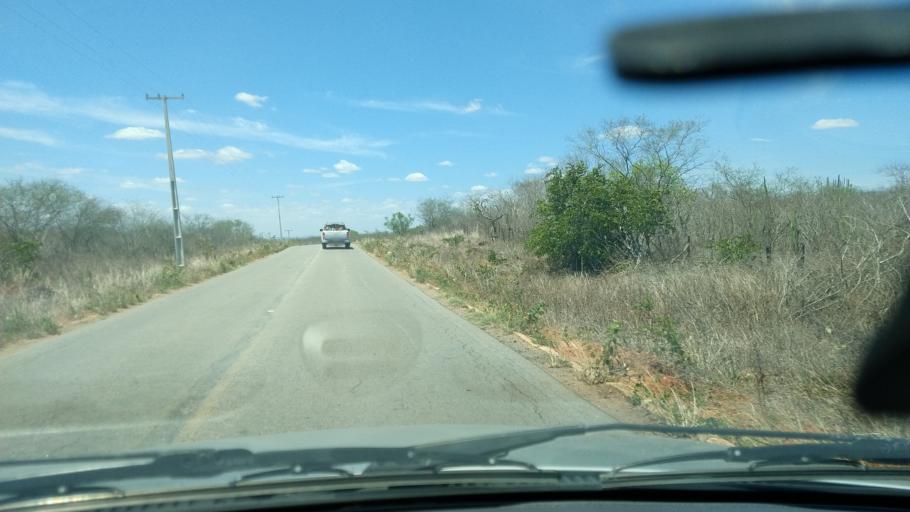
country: BR
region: Rio Grande do Norte
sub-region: Sao Paulo Do Potengi
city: Sao Paulo do Potengi
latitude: -5.9125
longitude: -35.5929
